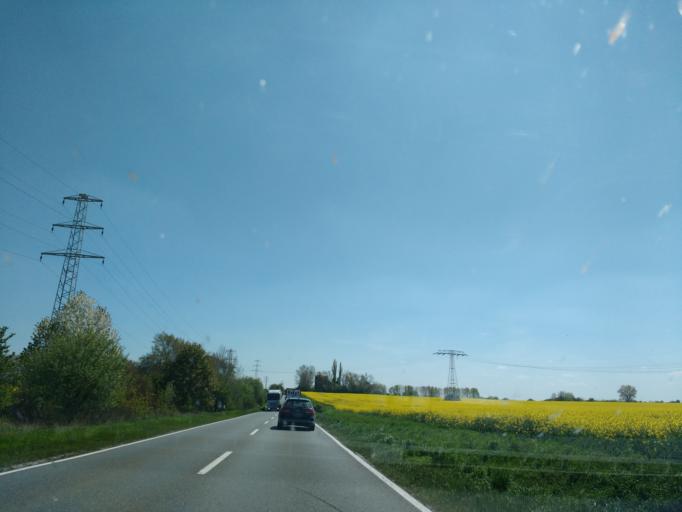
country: DE
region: Saxony-Anhalt
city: Deuben
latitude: 51.1061
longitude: 12.0914
